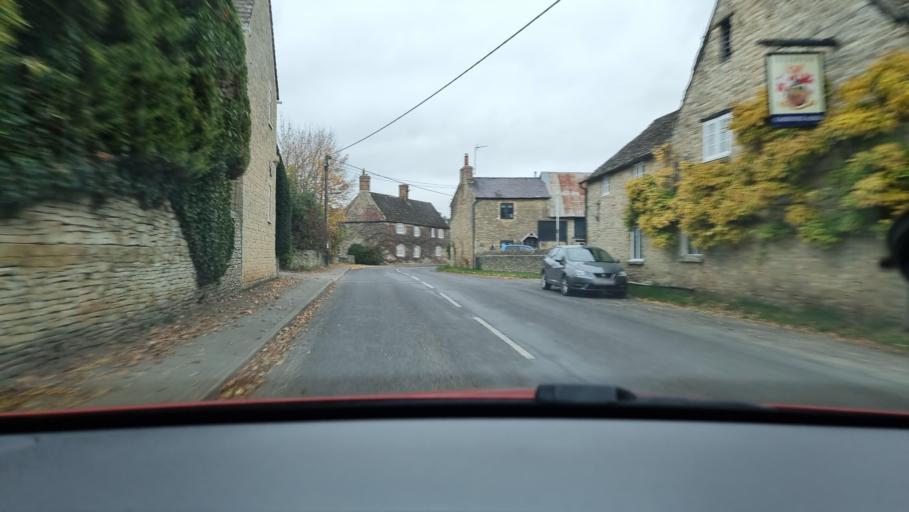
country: GB
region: England
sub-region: Oxfordshire
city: Woodstock
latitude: 51.8811
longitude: -1.3065
